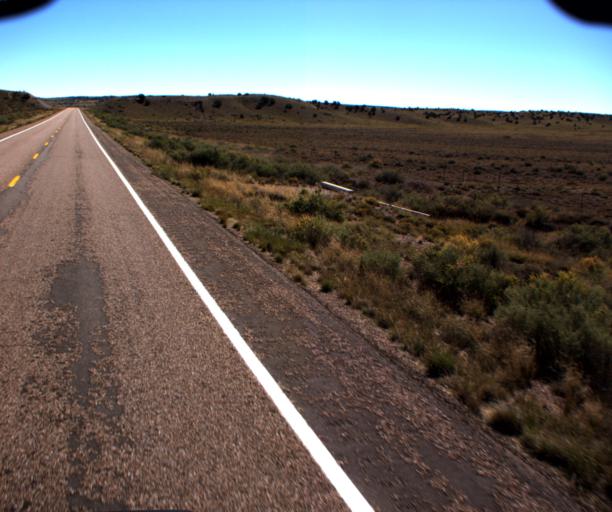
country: US
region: Arizona
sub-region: Apache County
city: Saint Johns
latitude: 34.5888
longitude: -109.5937
